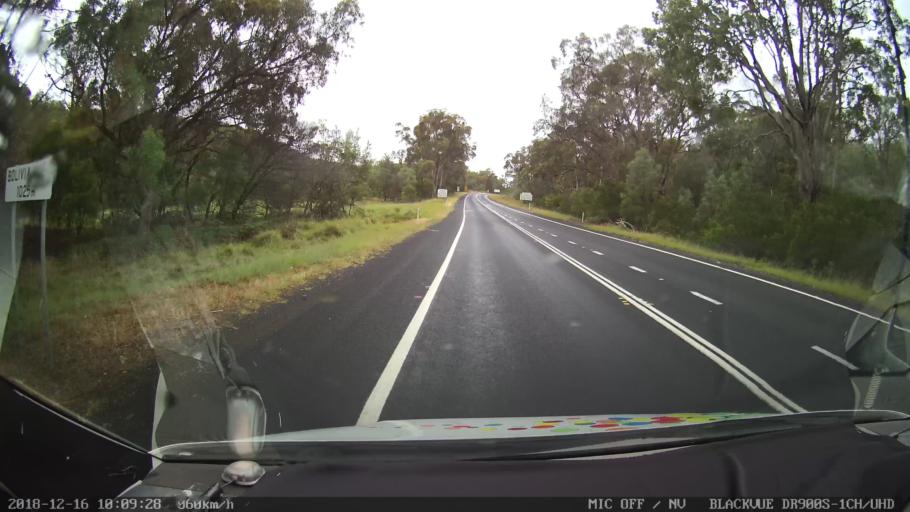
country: AU
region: New South Wales
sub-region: Glen Innes Severn
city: Glen Innes
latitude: -29.3238
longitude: 151.9165
